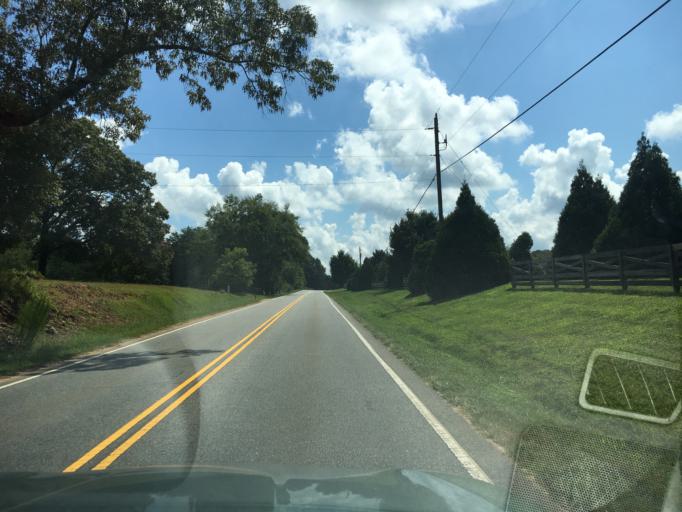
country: US
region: South Carolina
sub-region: Spartanburg County
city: Fairforest
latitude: 34.9084
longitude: -82.0495
